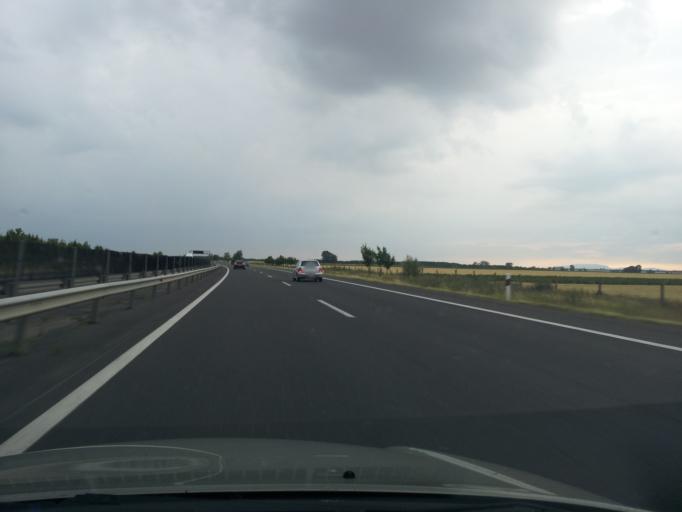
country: HU
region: Borsod-Abauj-Zemplen
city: Mezokeresztes
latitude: 47.8616
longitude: 20.7621
